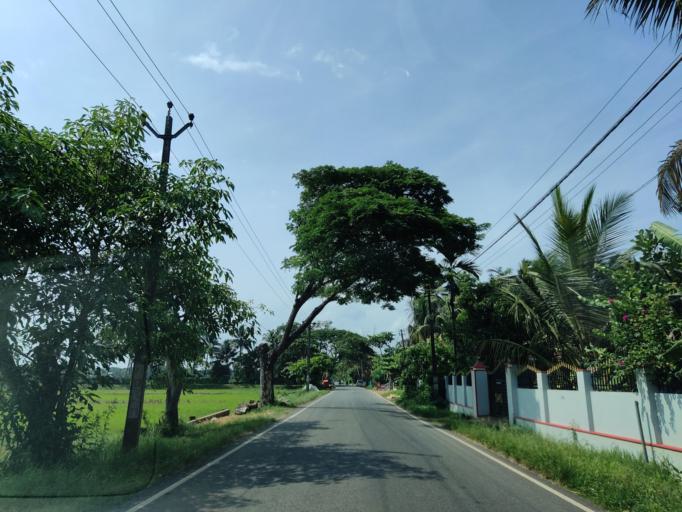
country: IN
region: Kerala
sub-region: Pattanamtitta
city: Tiruvalla
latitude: 9.3474
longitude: 76.4690
